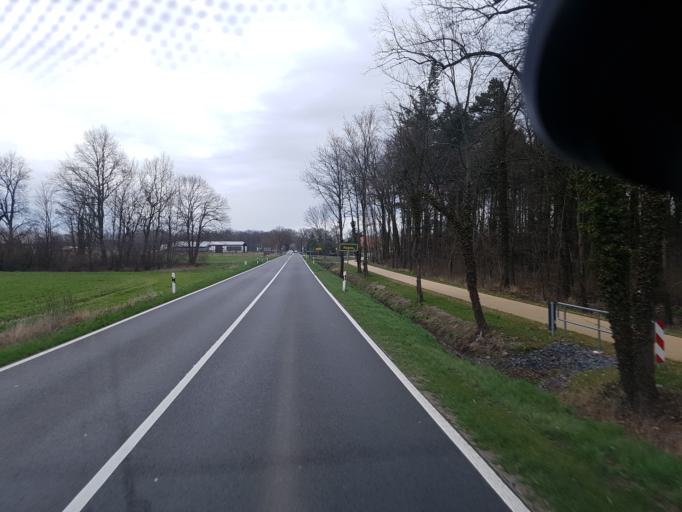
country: DE
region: Brandenburg
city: Beeskow
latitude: 52.1936
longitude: 14.2954
